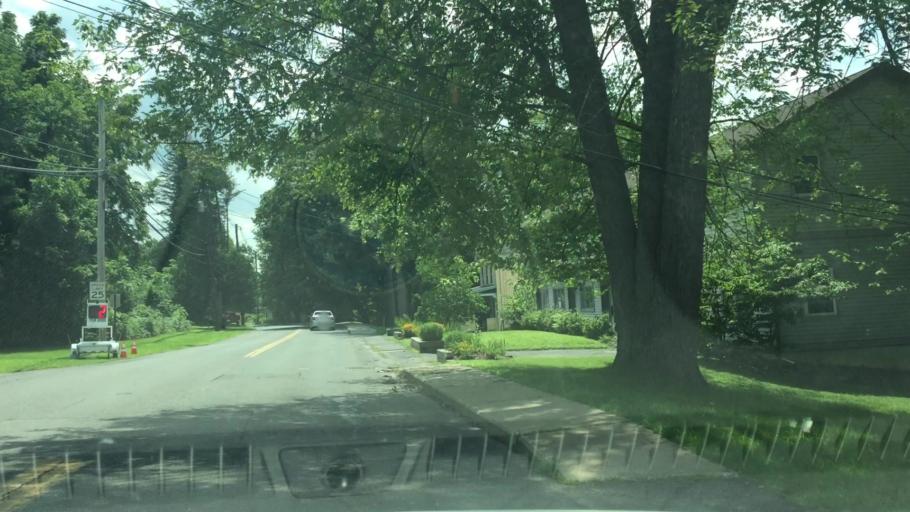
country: US
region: Massachusetts
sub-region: Berkshire County
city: Great Barrington
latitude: 42.1966
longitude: -73.3567
